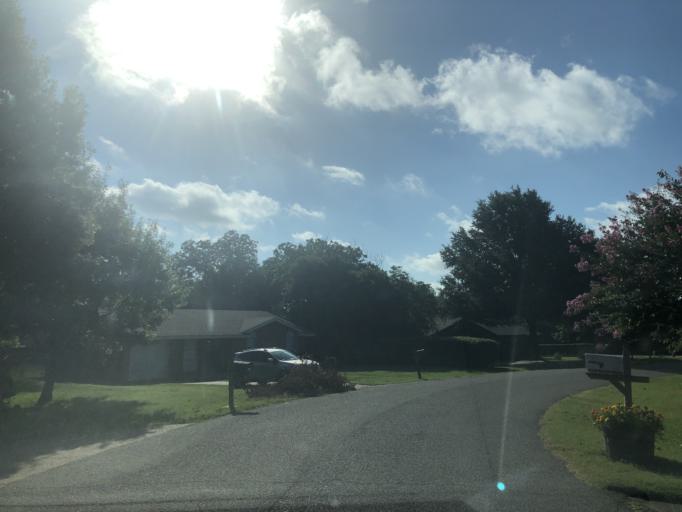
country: US
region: Texas
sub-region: Dallas County
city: Duncanville
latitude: 32.6598
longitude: -96.9233
